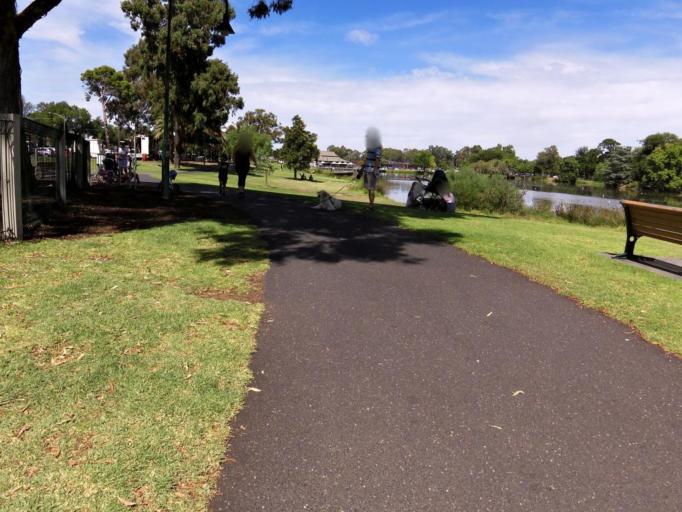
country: AU
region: Victoria
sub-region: Greater Bendigo
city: Bendigo
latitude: -36.7469
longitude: 144.2923
